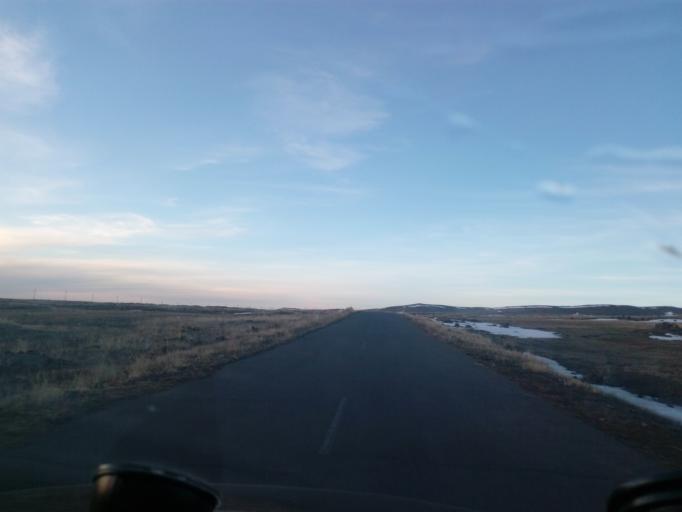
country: AM
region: Shirak
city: Lerrnakert
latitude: 40.4772
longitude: 43.9536
